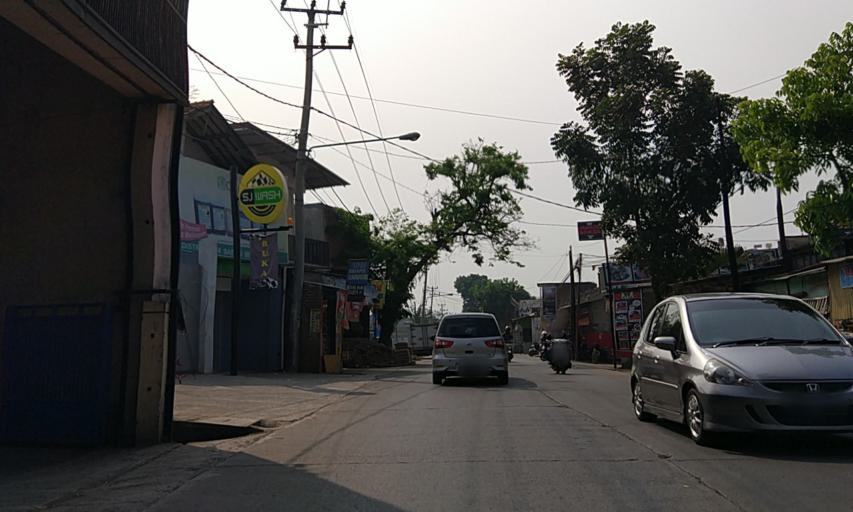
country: ID
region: West Java
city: Soreang
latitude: -7.0204
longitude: 107.5493
